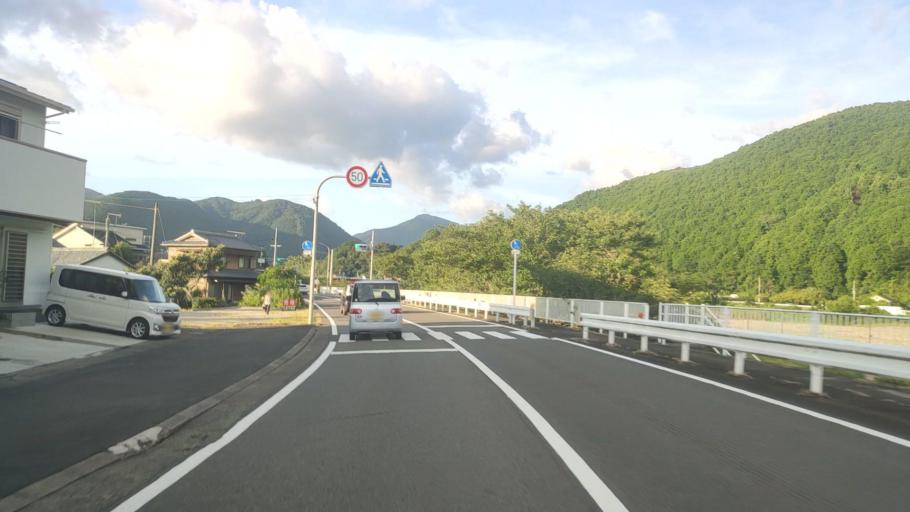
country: JP
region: Wakayama
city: Tanabe
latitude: 33.7193
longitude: 135.4809
